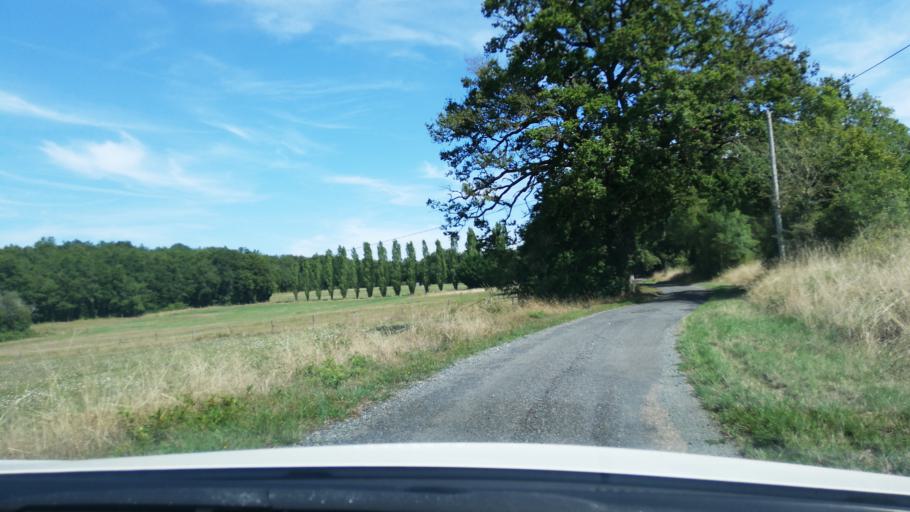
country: FR
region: Centre
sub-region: Departement d'Indre-et-Loire
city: Mazieres-de-Touraine
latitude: 47.3967
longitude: 0.4438
